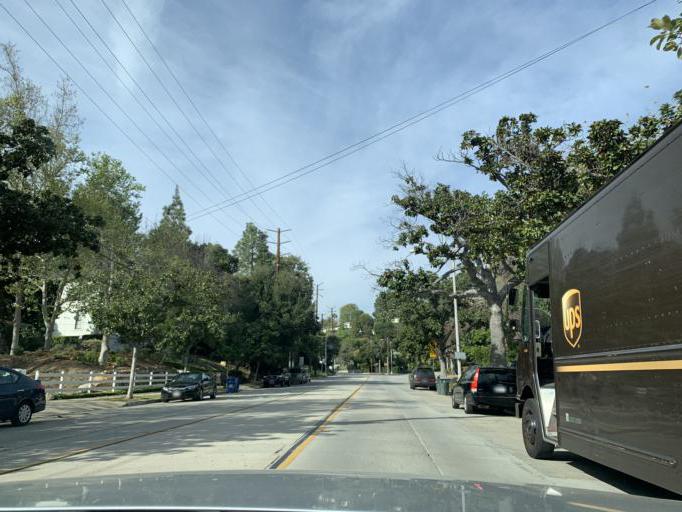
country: US
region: California
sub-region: Los Angeles County
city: South Pasadena
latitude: 34.1260
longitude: -118.1766
